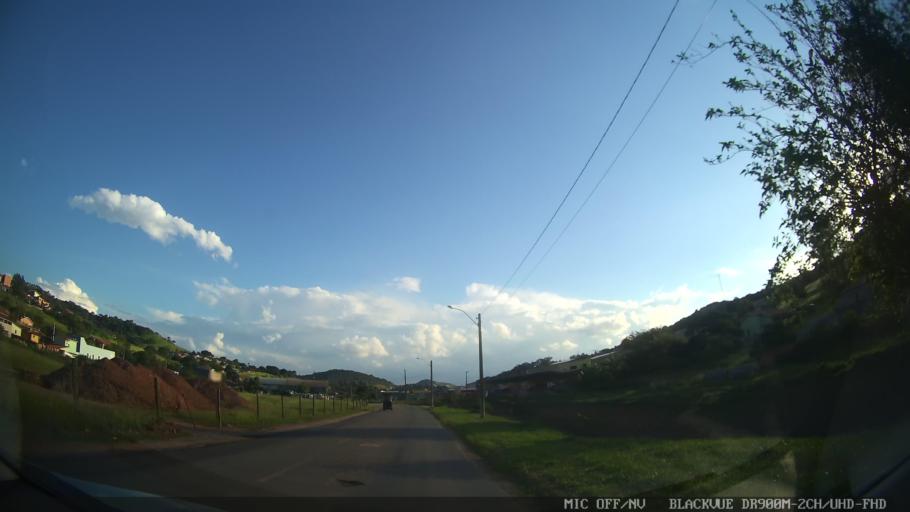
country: BR
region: Minas Gerais
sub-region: Extrema
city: Extrema
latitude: -22.8940
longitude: -46.4205
